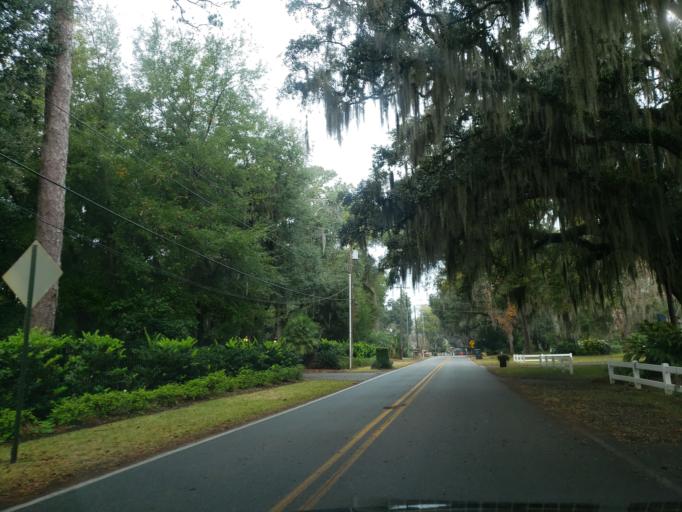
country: US
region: Georgia
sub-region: Chatham County
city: Wilmington Island
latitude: 31.9738
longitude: -81.0001
